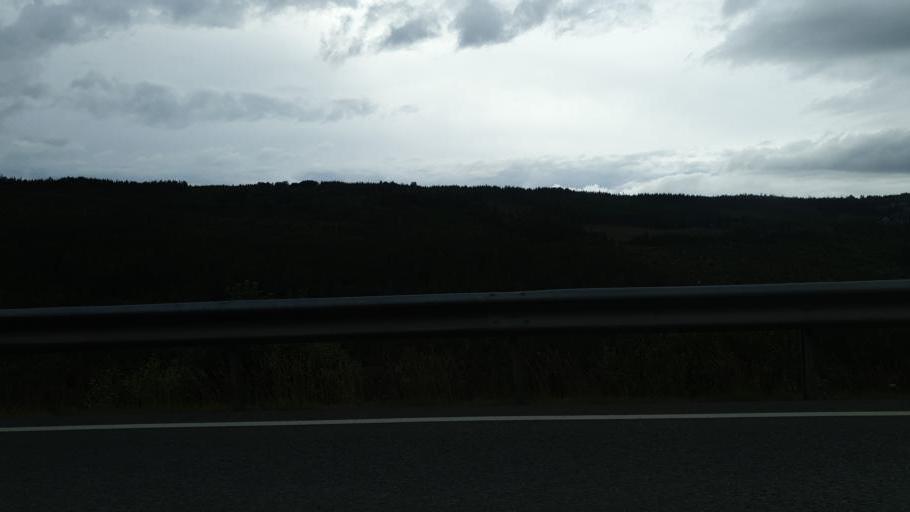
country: NO
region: Sor-Trondelag
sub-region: Rennebu
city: Berkak
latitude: 62.7433
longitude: 9.9789
